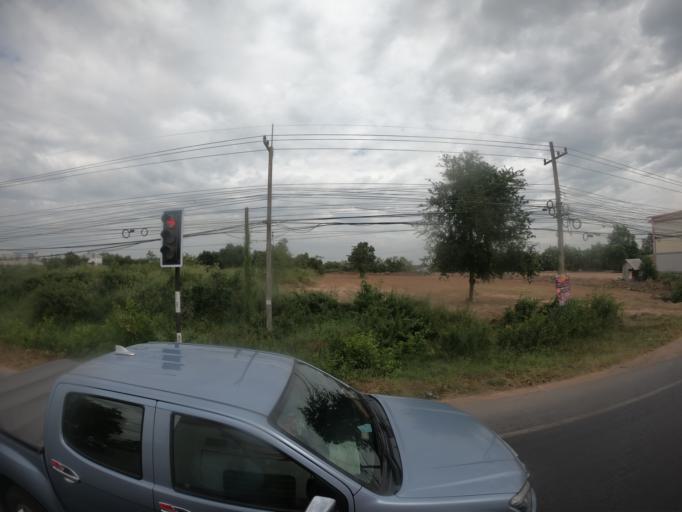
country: TH
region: Maha Sarakham
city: Maha Sarakham
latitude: 16.2081
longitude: 103.2852
